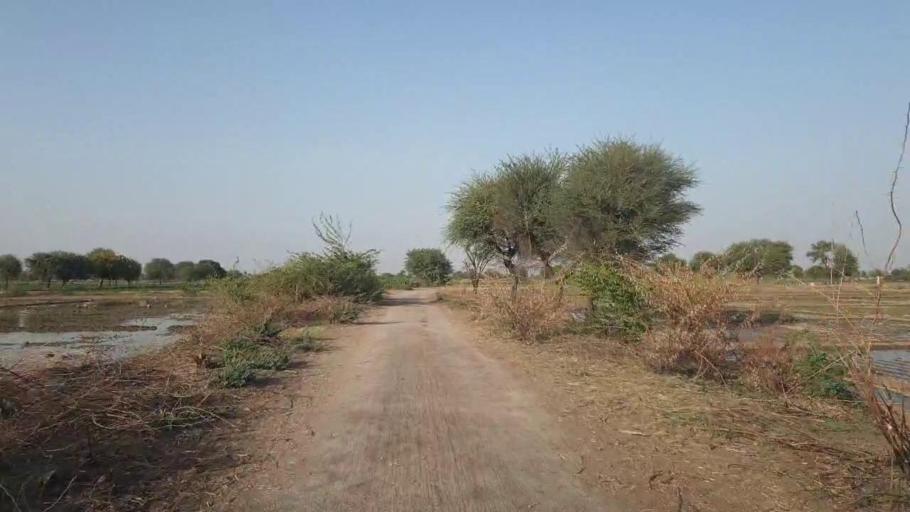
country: PK
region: Sindh
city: Dhoro Naro
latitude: 25.4942
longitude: 69.5760
